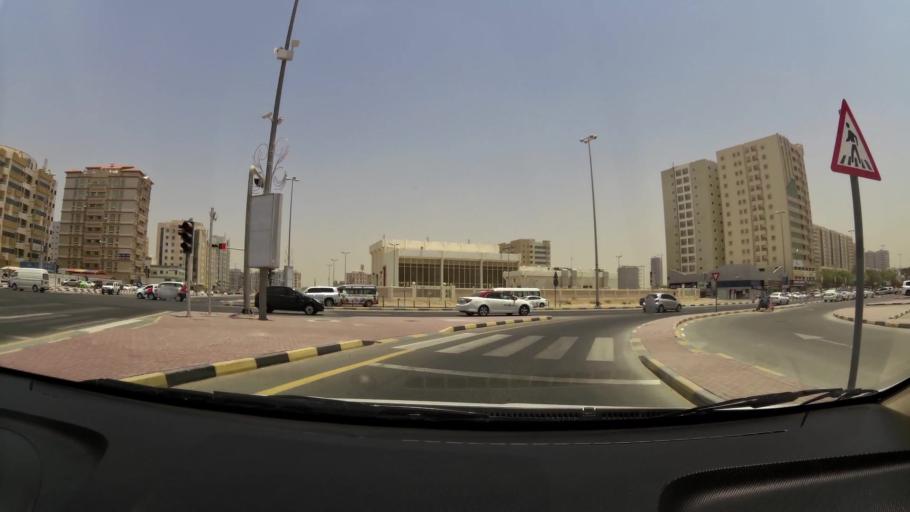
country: AE
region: Ajman
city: Ajman
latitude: 25.4090
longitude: 55.5072
